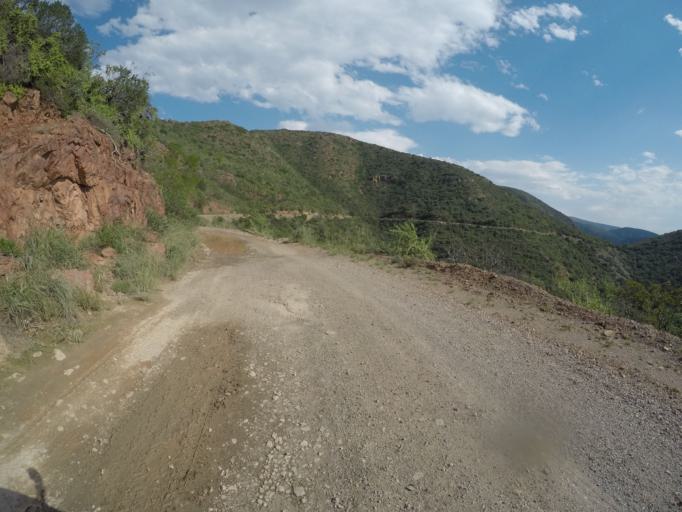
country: ZA
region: Eastern Cape
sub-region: Cacadu District Municipality
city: Kareedouw
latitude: -33.6472
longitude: 24.3448
